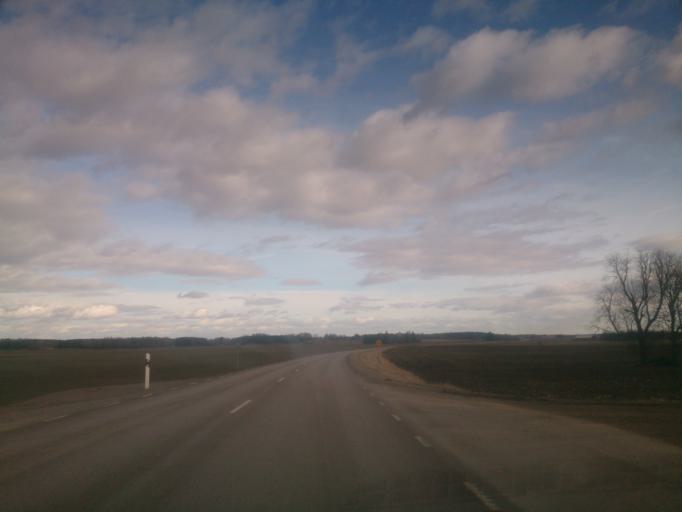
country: SE
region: OEstergoetland
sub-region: Motala Kommun
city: Borensberg
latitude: 58.4955
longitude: 15.3405
